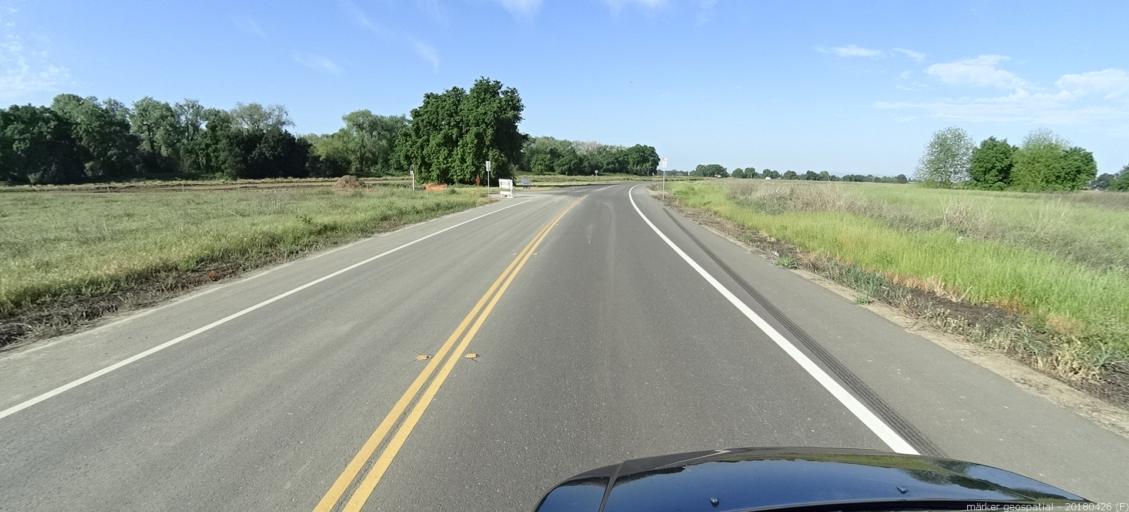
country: US
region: California
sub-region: Yolo County
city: West Sacramento
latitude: 38.5384
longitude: -121.5224
